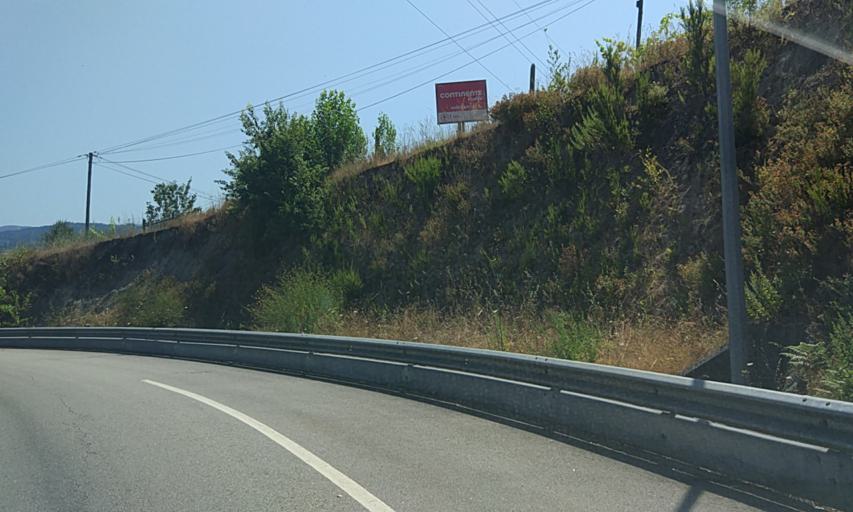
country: PT
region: Porto
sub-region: Amarante
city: Amarante
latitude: 41.2675
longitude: -8.0935
